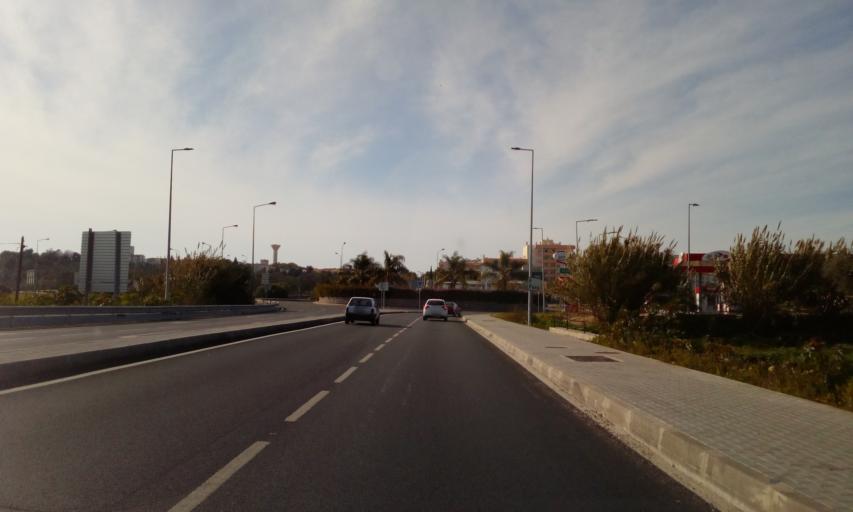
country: PT
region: Faro
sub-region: Faro
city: Faro
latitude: 37.0266
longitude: -7.9160
